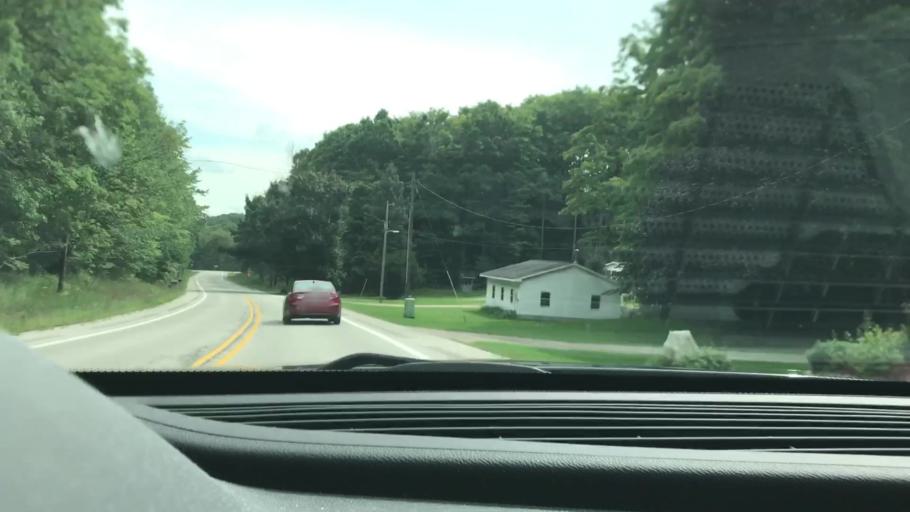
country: US
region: Michigan
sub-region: Antrim County
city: Bellaire
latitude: 45.0826
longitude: -85.2854
